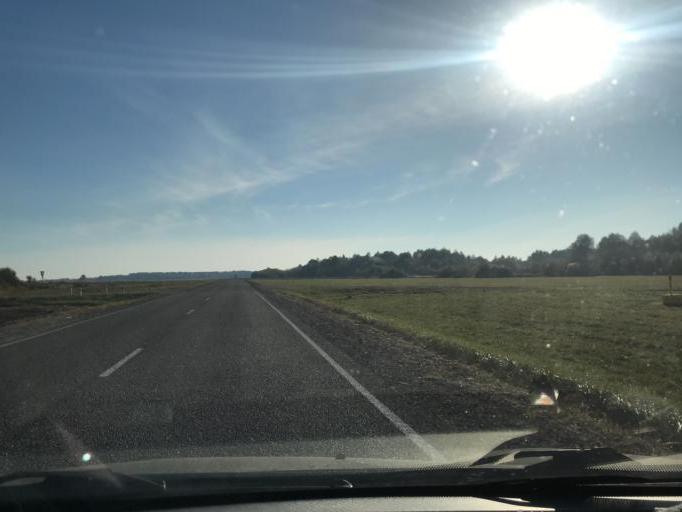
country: BY
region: Gomel
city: Brahin
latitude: 51.7735
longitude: 30.2682
